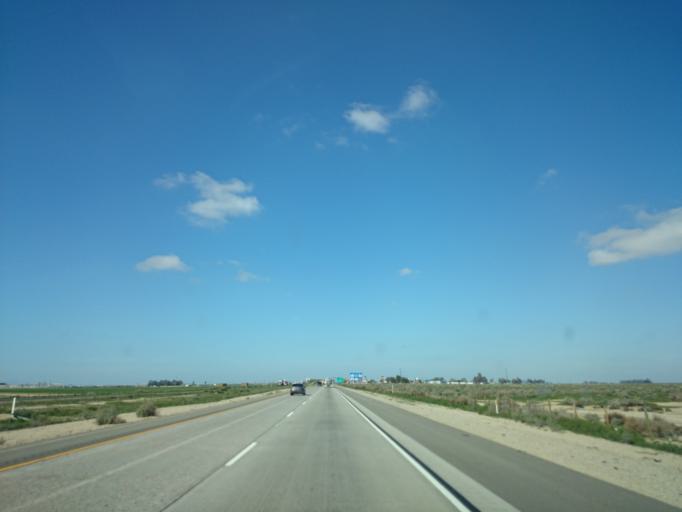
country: US
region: California
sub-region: Kern County
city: Buttonwillow
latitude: 35.3909
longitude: -119.3860
